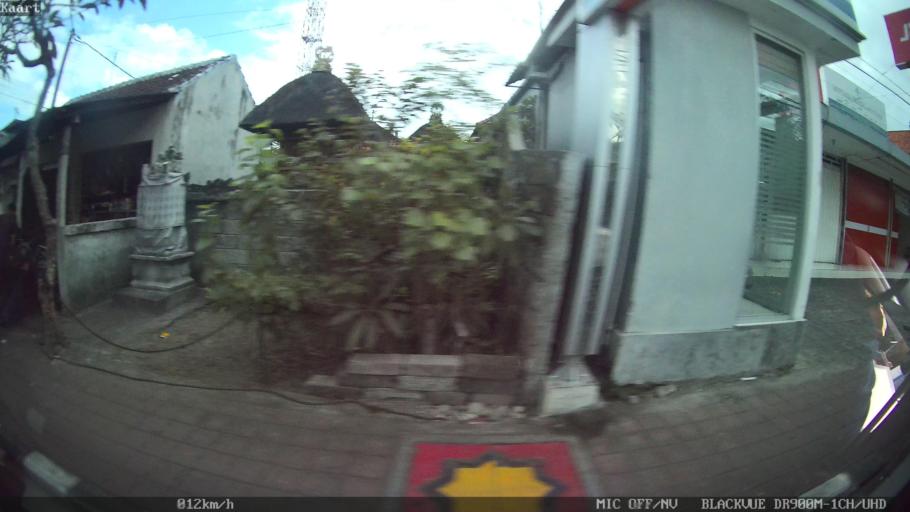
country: ID
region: Bali
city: Banjar Pekenjelodan
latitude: -8.5838
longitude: 115.1802
